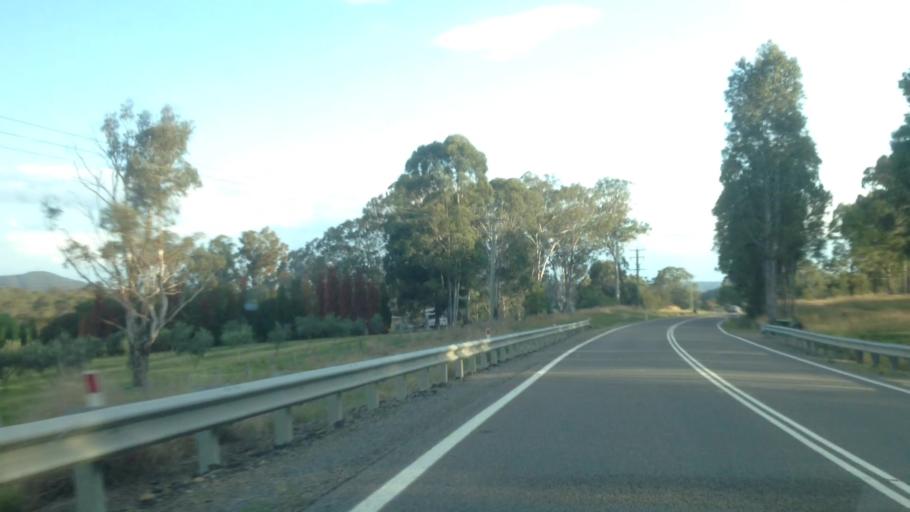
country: AU
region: New South Wales
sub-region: Cessnock
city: Kurri Kurri
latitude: -32.8693
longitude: 151.4794
